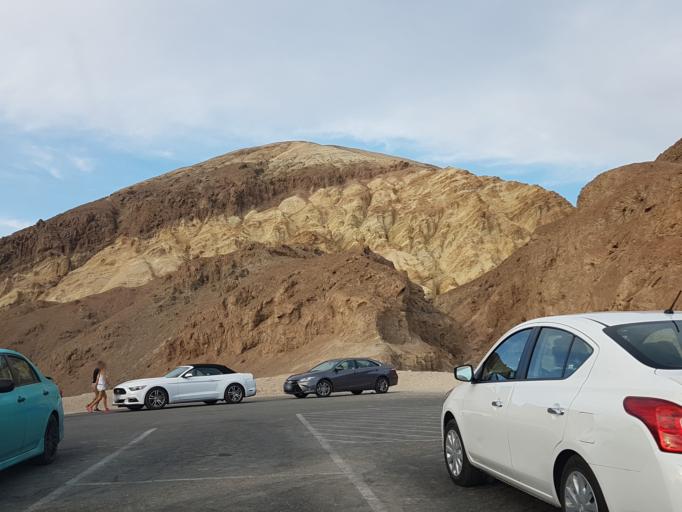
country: US
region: Nevada
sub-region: Nye County
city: Beatty
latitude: 36.4205
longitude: -116.8469
